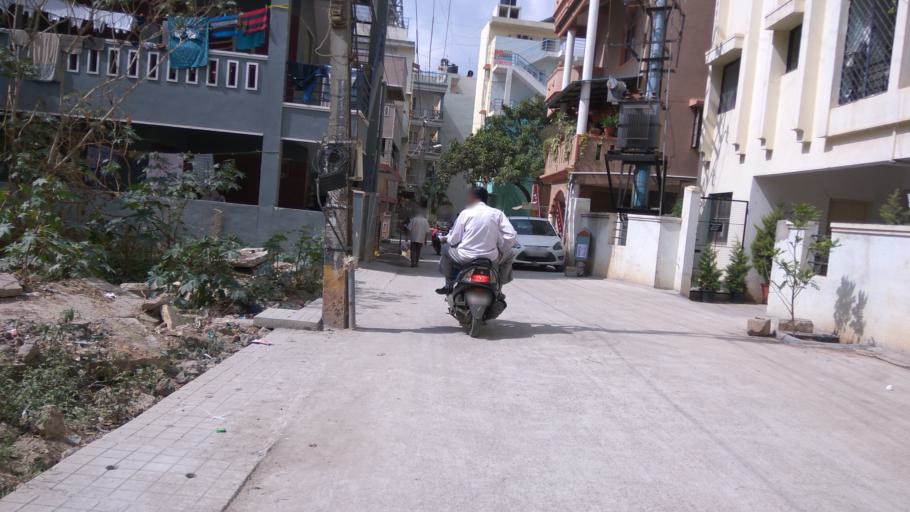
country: IN
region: Karnataka
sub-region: Bangalore Urban
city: Bangalore
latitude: 12.9547
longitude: 77.6919
